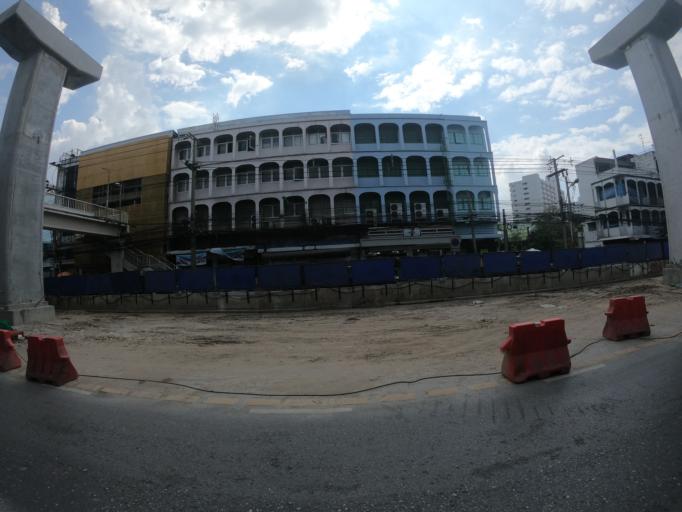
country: TH
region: Bangkok
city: Lat Phrao
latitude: 13.7941
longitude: 100.5950
